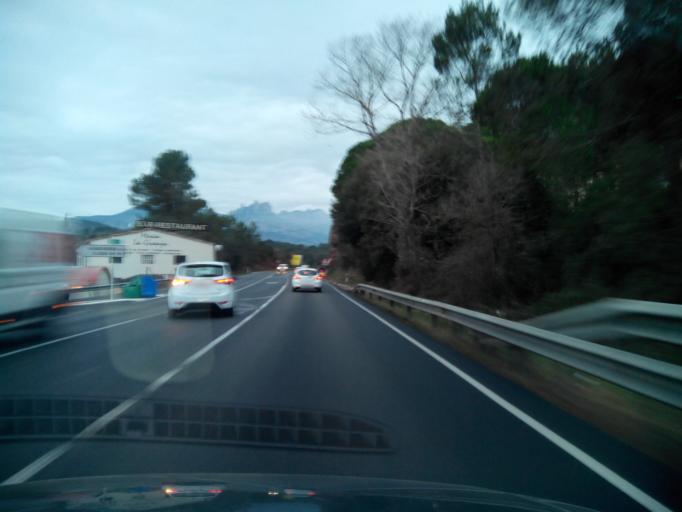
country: ES
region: Catalonia
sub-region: Provincia de Barcelona
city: Viladecavalls
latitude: 41.5862
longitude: 1.9212
